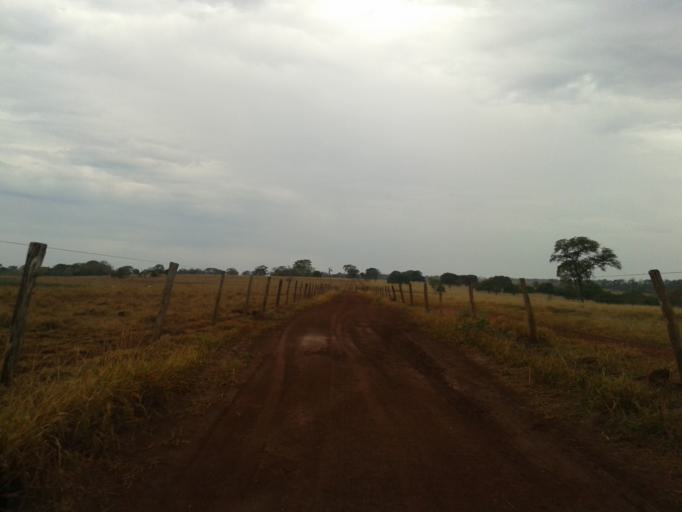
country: BR
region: Minas Gerais
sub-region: Santa Vitoria
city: Santa Vitoria
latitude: -18.8677
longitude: -49.8229
